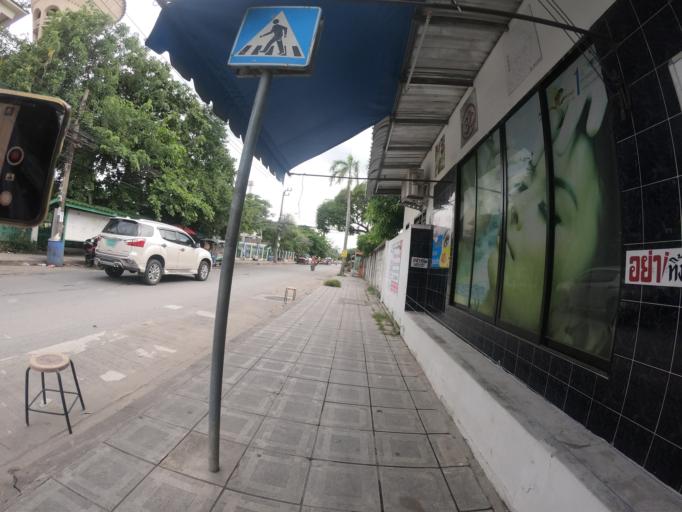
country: TH
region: Bangkok
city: Suan Luang
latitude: 13.7101
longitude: 100.6617
